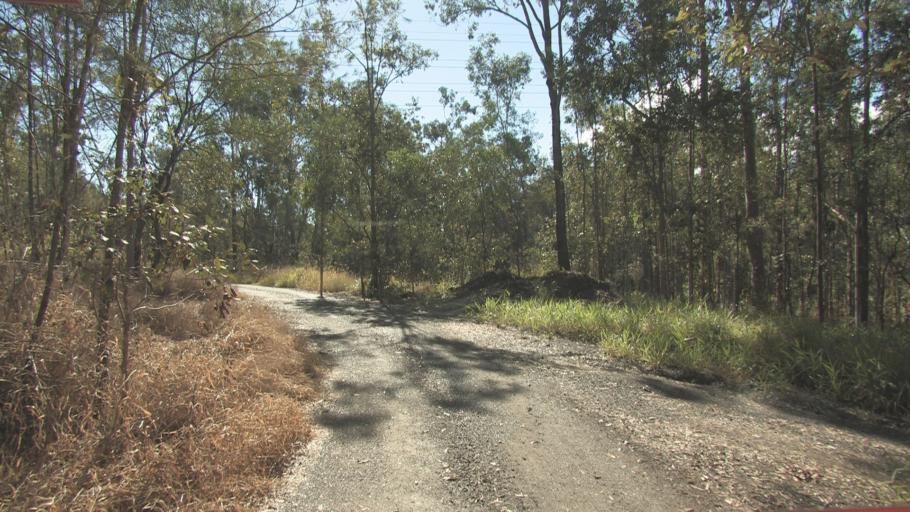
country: AU
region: Queensland
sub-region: Logan
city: Chambers Flat
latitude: -27.8037
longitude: 153.0878
